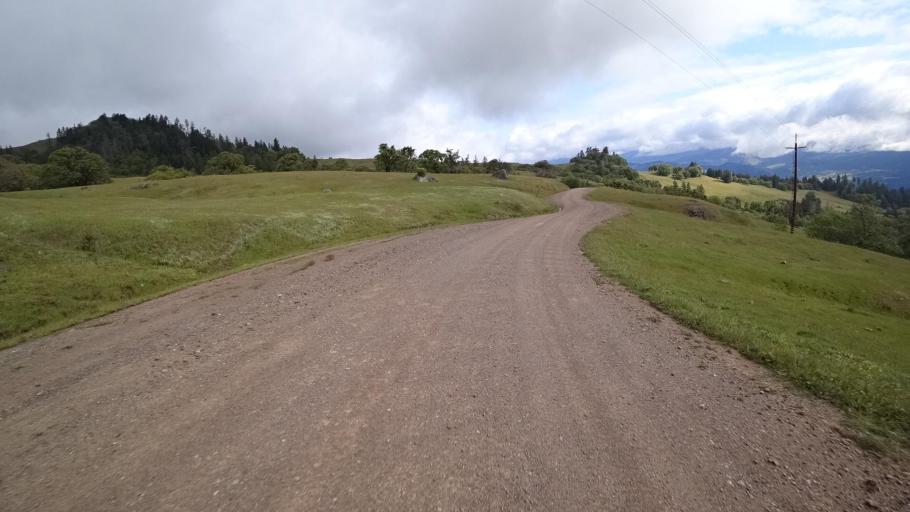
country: US
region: California
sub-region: Humboldt County
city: Redway
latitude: 40.2029
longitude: -123.6943
